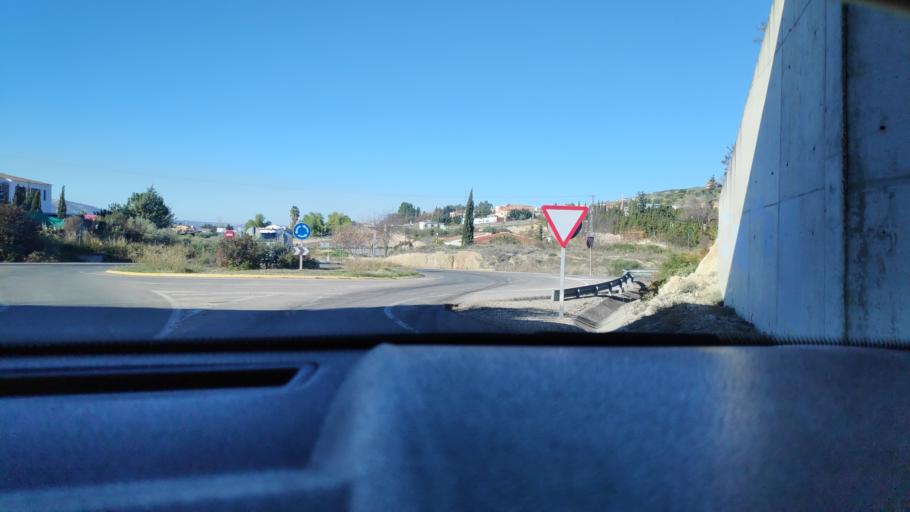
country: ES
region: Andalusia
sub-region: Province of Cordoba
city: Baena
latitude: 37.6232
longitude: -4.3007
